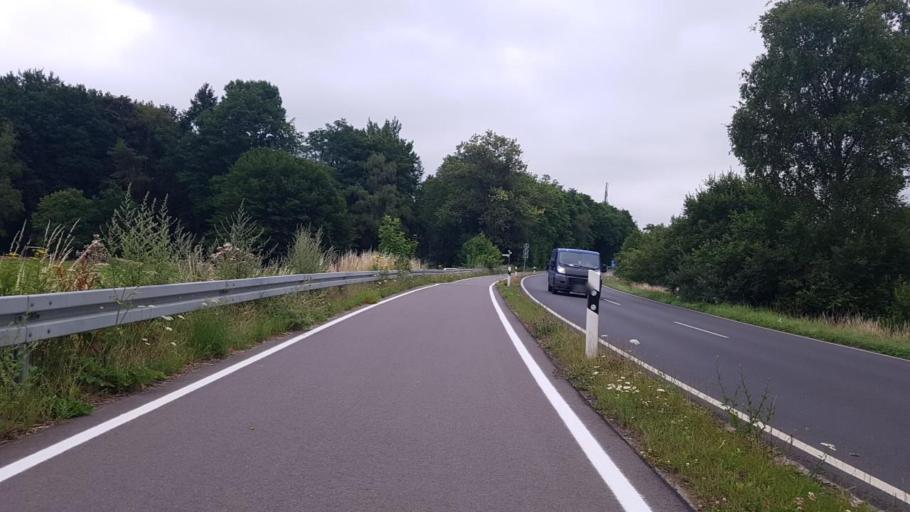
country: DE
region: North Rhine-Westphalia
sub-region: Regierungsbezirk Koln
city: Wurselen
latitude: 50.7909
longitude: 6.1755
